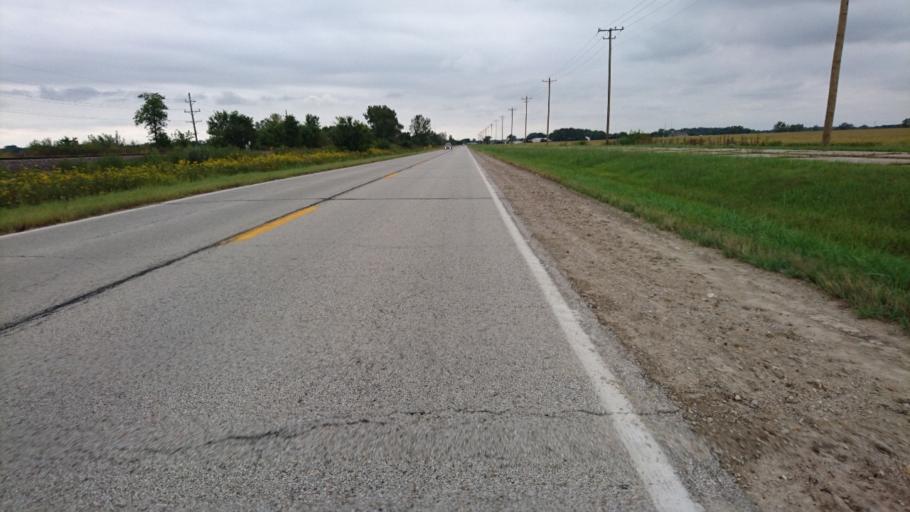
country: US
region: Illinois
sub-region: Livingston County
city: Pontiac
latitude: 40.9082
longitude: -88.6140
